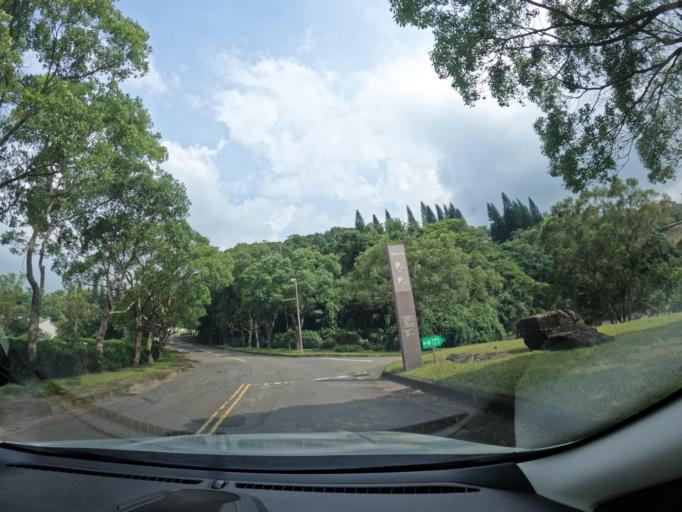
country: TW
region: Taiwan
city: Daxi
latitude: 24.8827
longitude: 121.3237
